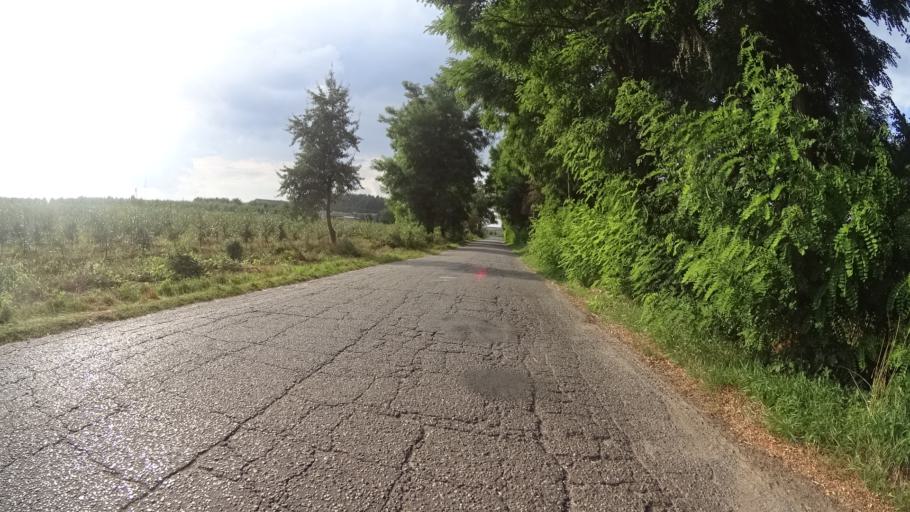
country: PL
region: Masovian Voivodeship
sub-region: Powiat grojecki
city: Mogielnica
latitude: 51.6668
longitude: 20.7407
